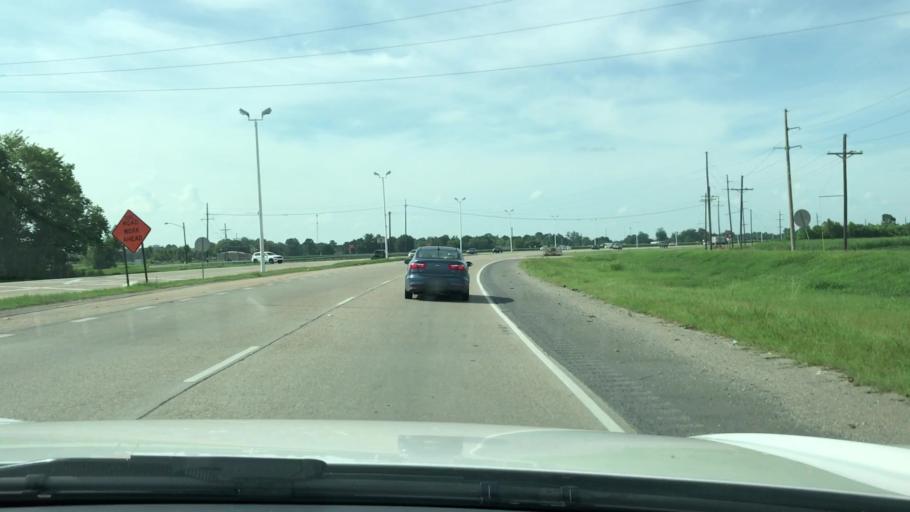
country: US
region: Louisiana
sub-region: West Baton Rouge Parish
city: Addis
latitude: 30.3407
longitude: -91.2604
